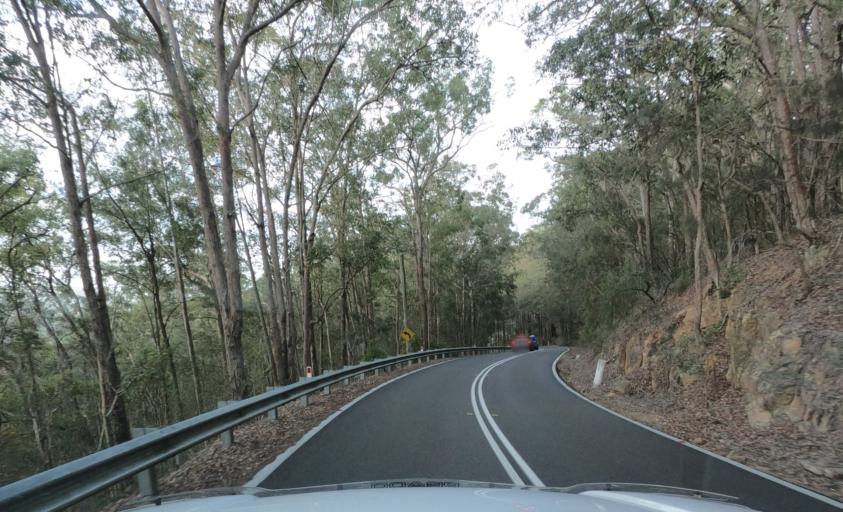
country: AU
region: New South Wales
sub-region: Wyong Shire
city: Little Jilliby
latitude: -33.2276
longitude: 151.2722
